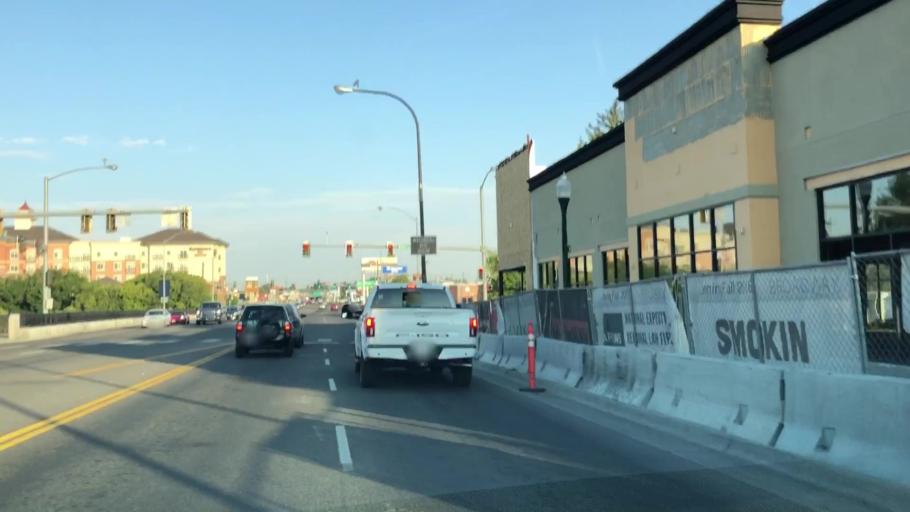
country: US
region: Idaho
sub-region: Bonneville County
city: Idaho Falls
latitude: 43.4925
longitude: -112.0432
